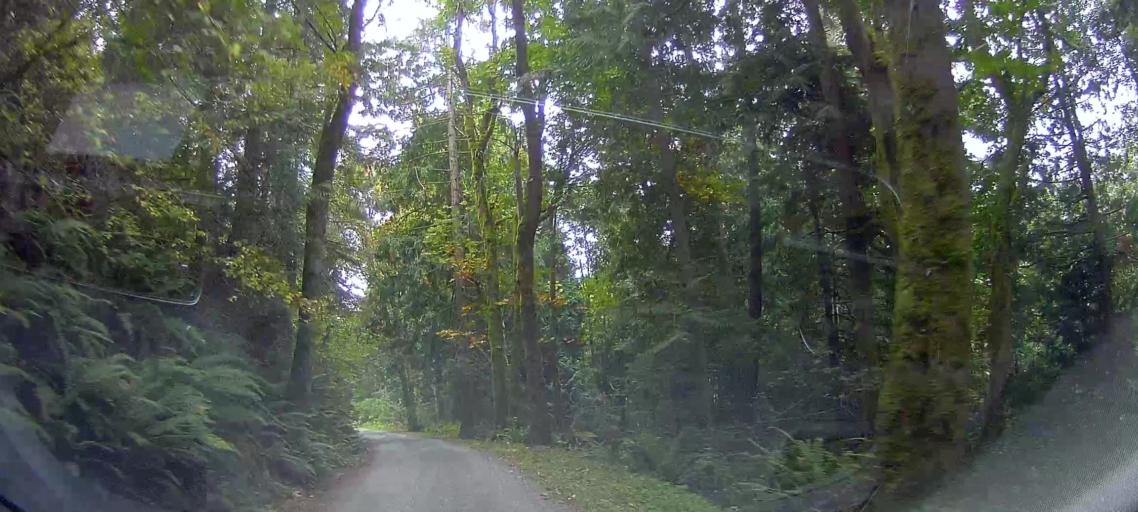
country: US
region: Washington
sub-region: Whatcom County
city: Geneva
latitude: 48.6183
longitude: -122.4377
